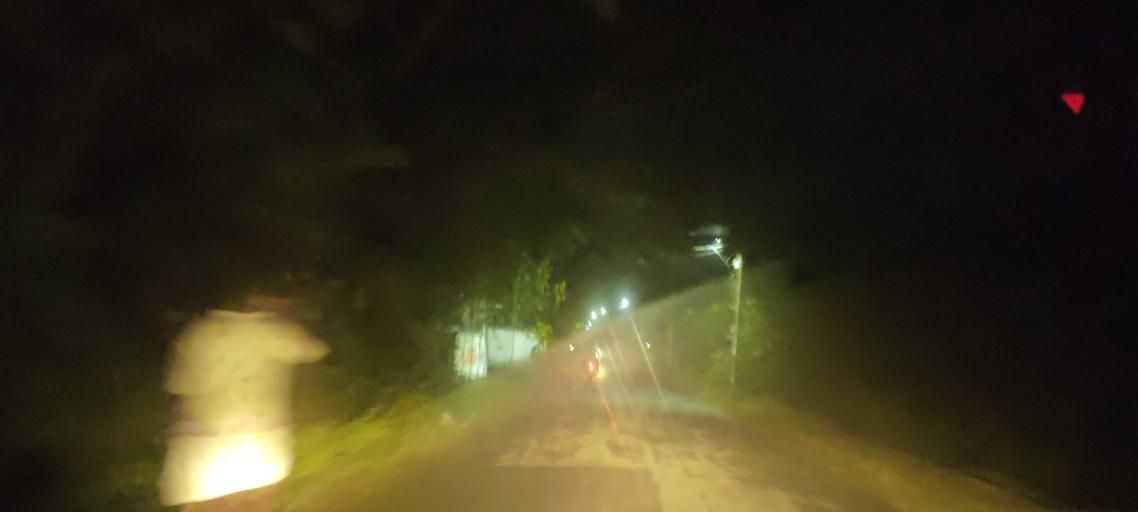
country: IN
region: Kerala
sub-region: Alappuzha
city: Vayalar
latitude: 9.7236
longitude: 76.3333
